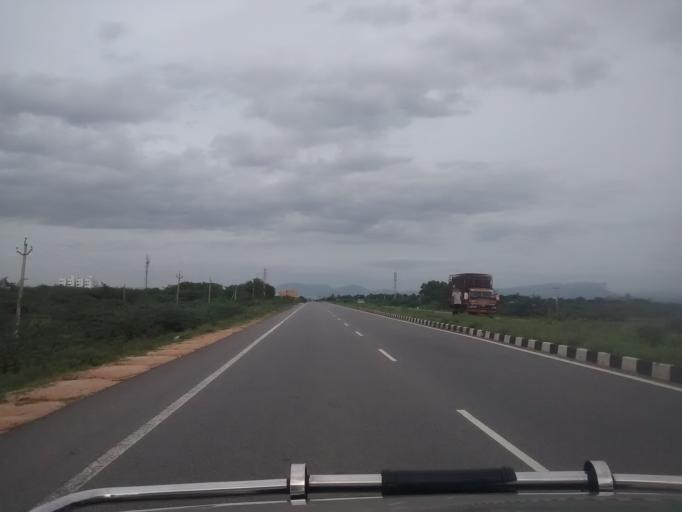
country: IN
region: Andhra Pradesh
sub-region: Chittoor
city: Tirupati
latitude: 13.6044
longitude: 79.3857
